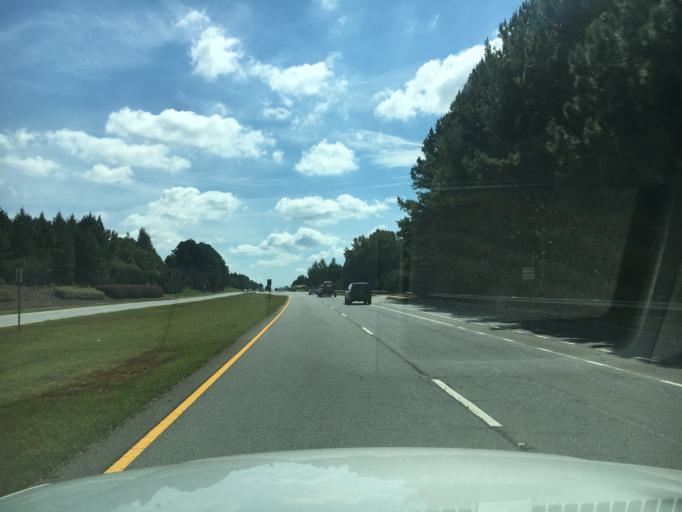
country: US
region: Georgia
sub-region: Gwinnett County
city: Duluth
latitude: 34.0046
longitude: -84.0979
